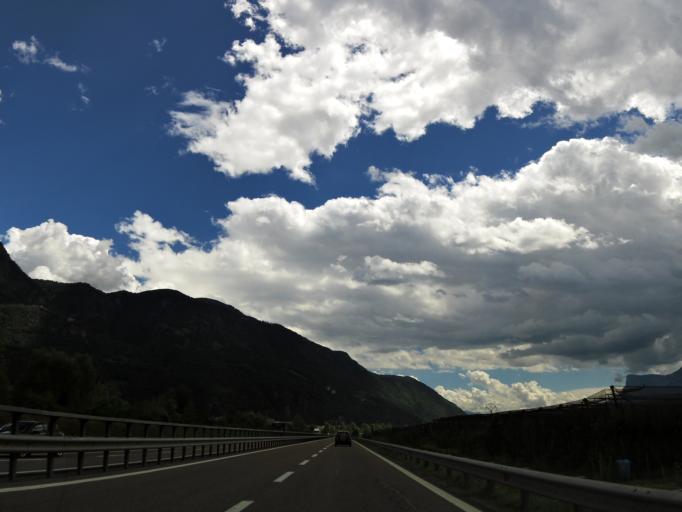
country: IT
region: Trentino-Alto Adige
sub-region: Bolzano
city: Sinigo
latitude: 46.6432
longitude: 11.1637
